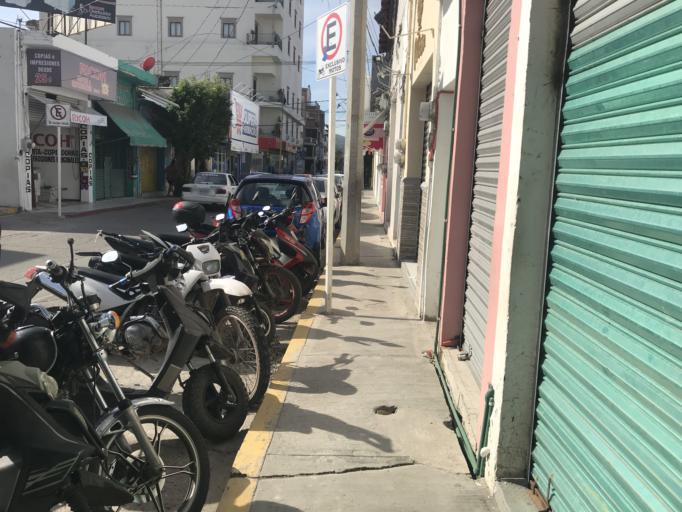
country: MX
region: Guerrero
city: Iguala de la Independencia
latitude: 18.3452
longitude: -99.5374
